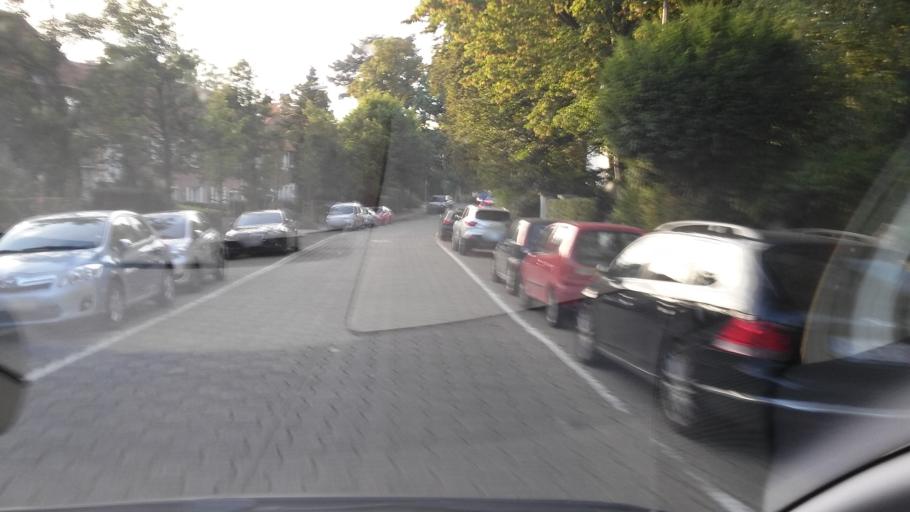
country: BE
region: Flanders
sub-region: Provincie Vlaams-Brabant
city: Hoeilaart
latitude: 50.8040
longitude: 4.4104
